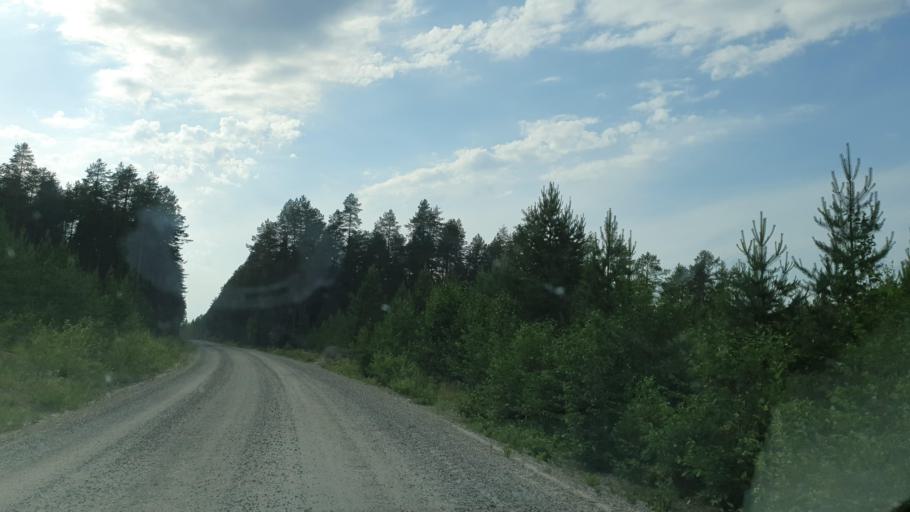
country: FI
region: Kainuu
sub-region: Kehys-Kainuu
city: Kuhmo
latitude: 64.0946
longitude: 29.6440
